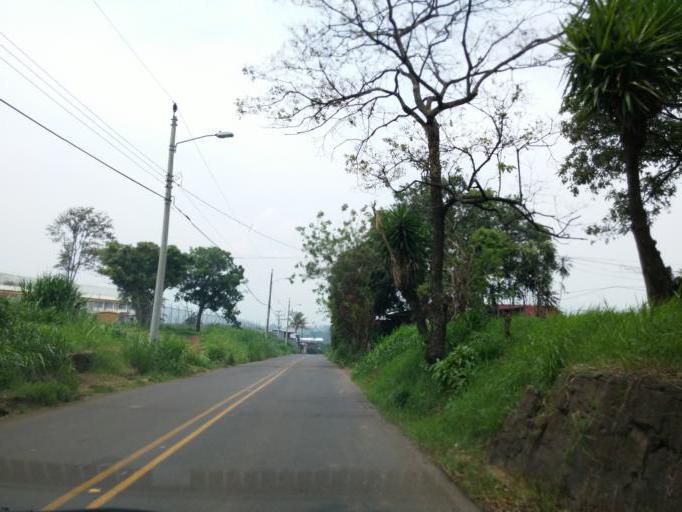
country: CR
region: Heredia
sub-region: Canton de Belen
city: San Antonio
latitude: 9.9953
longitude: -84.1998
